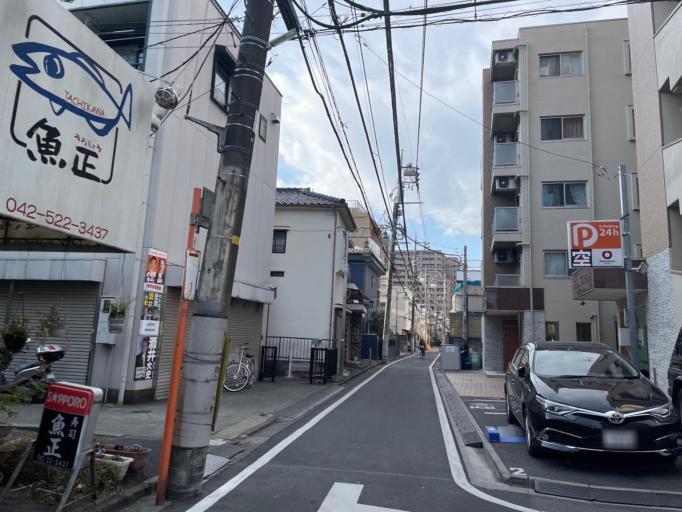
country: JP
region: Tokyo
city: Hino
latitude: 35.7013
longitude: 139.4181
